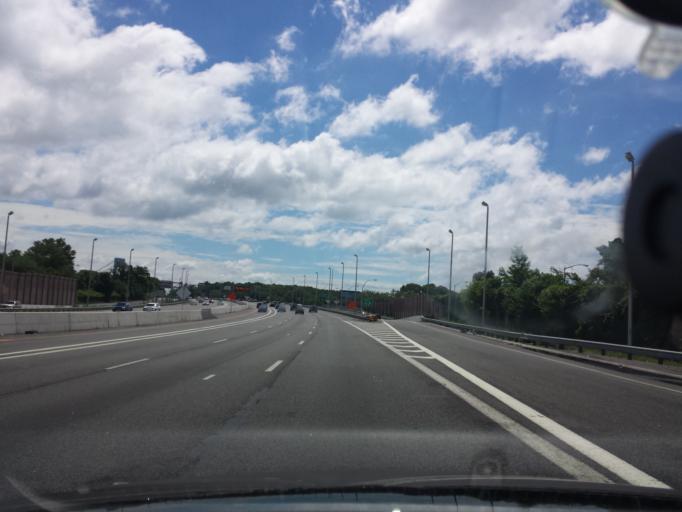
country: US
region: New Jersey
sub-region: Hudson County
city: Bayonne
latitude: 40.6072
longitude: -74.0865
